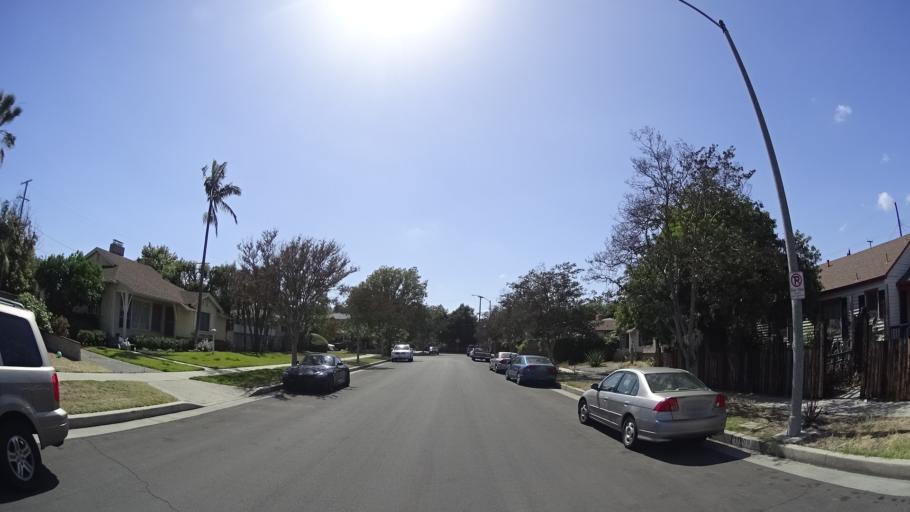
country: US
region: California
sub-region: Los Angeles County
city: North Hollywood
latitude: 34.1786
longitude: -118.3924
